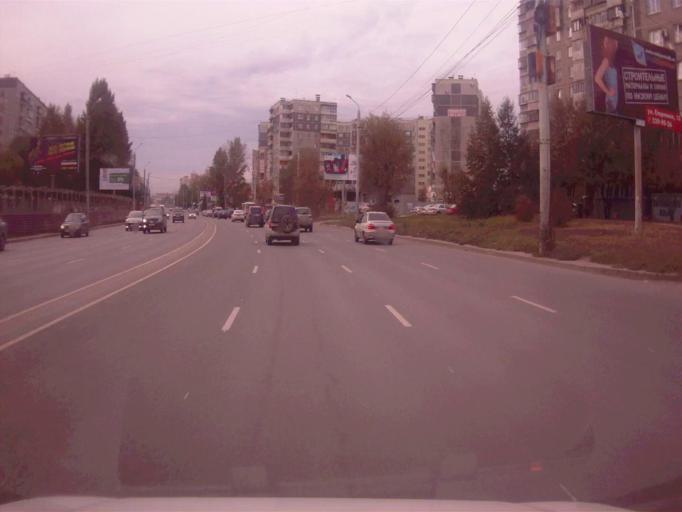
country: RU
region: Chelyabinsk
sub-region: Gorod Chelyabinsk
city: Chelyabinsk
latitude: 55.1786
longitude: 61.3700
